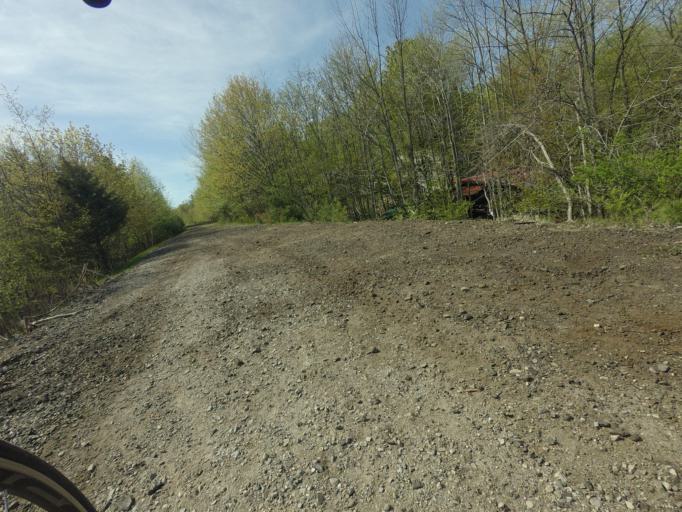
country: CA
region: Ontario
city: Arnprior
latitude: 45.4643
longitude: -76.2852
